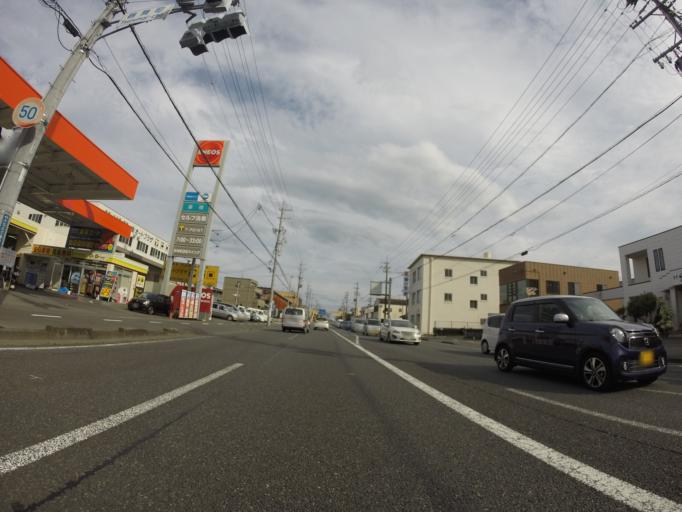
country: JP
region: Shizuoka
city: Shizuoka-shi
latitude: 35.0172
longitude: 138.4757
